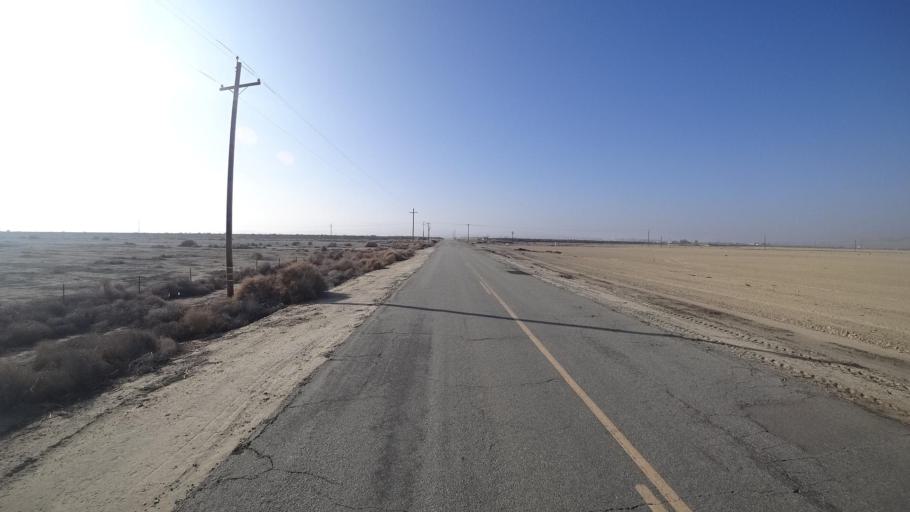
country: US
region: California
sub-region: Kern County
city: Maricopa
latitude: 35.1012
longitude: -119.3647
